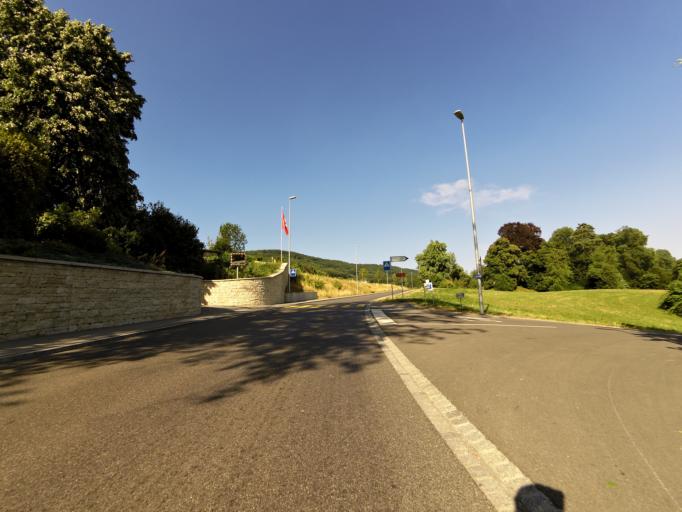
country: CH
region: Aargau
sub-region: Bezirk Lenzburg
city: Niederlenz
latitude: 47.4181
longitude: 8.1697
